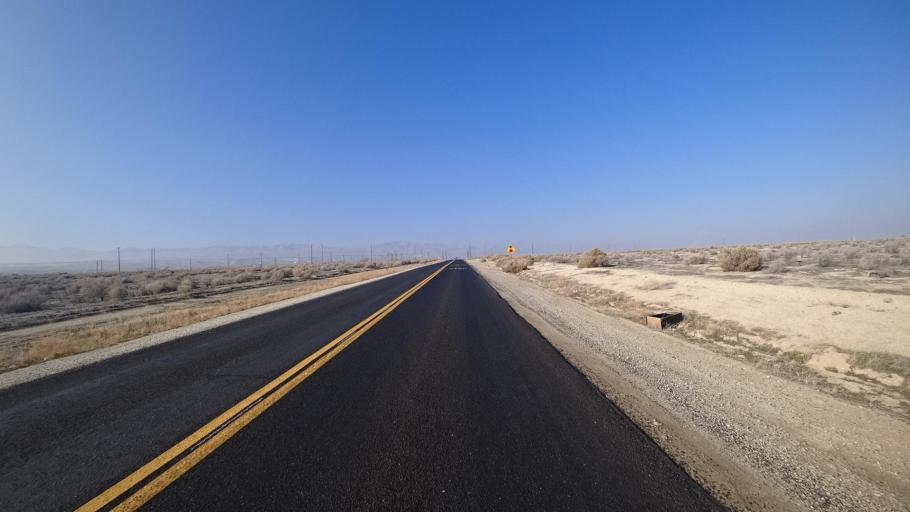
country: US
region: California
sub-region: Kern County
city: Taft Heights
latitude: 35.1803
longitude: -119.5233
